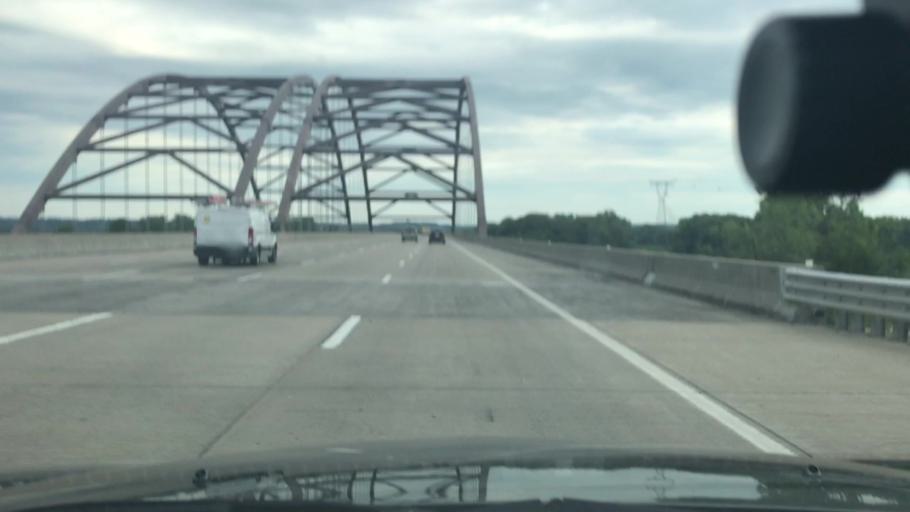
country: US
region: Missouri
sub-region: Saint Charles County
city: Saint Charles
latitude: 38.7386
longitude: -90.5242
